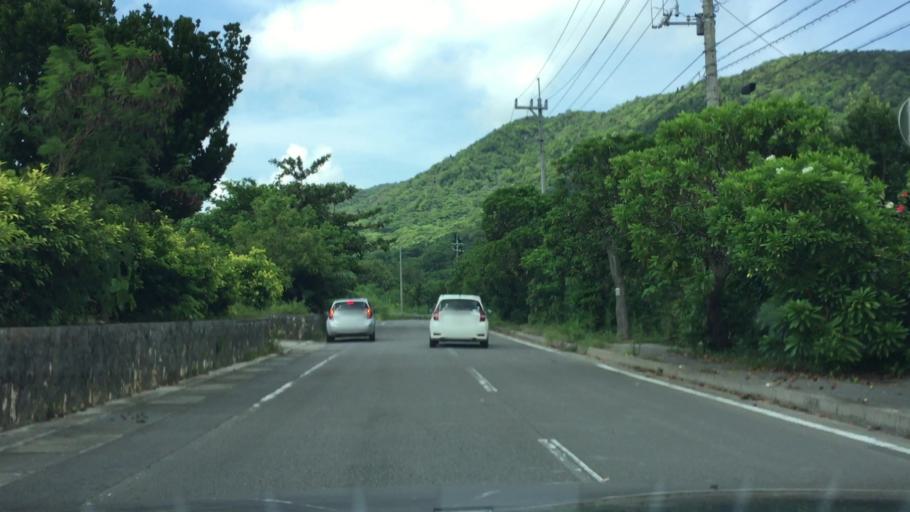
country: JP
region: Okinawa
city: Ishigaki
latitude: 24.4551
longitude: 124.2244
